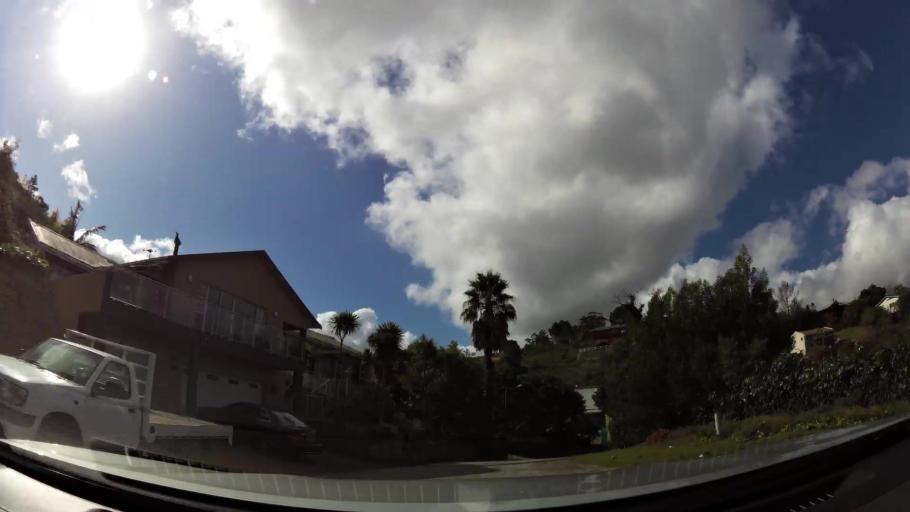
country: ZA
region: Western Cape
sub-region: Eden District Municipality
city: Knysna
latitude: -34.0520
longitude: 23.0833
